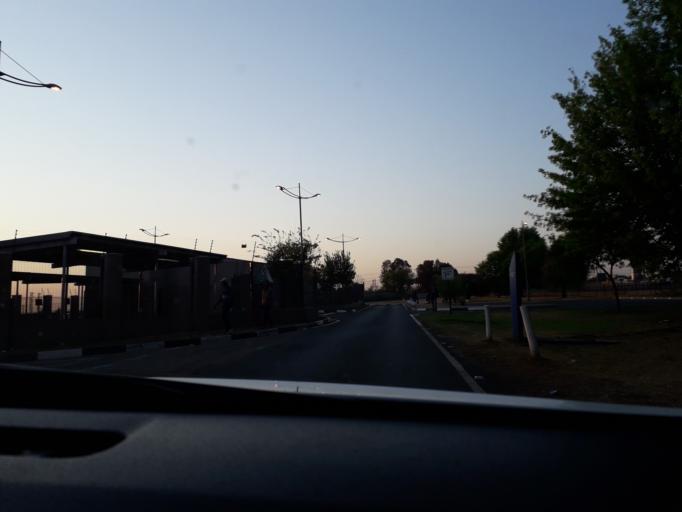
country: ZA
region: Gauteng
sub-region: Ekurhuleni Metropolitan Municipality
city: Tembisa
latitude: -26.0065
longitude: 28.2537
